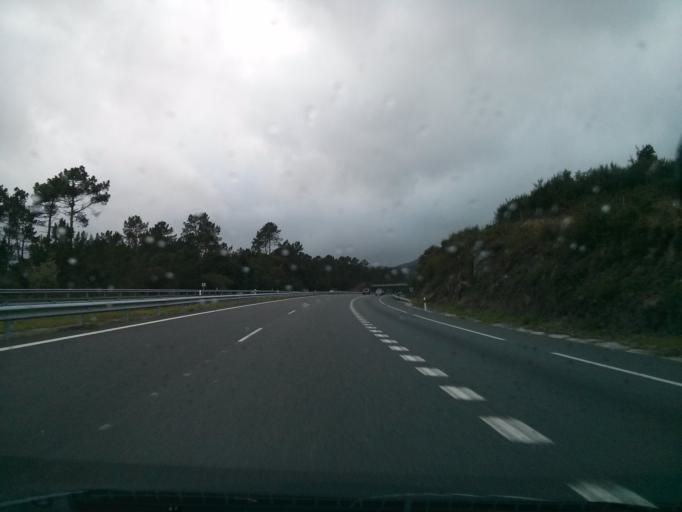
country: ES
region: Galicia
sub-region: Provincia de Ourense
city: Carballeda de Avia
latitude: 42.2948
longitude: -8.1889
